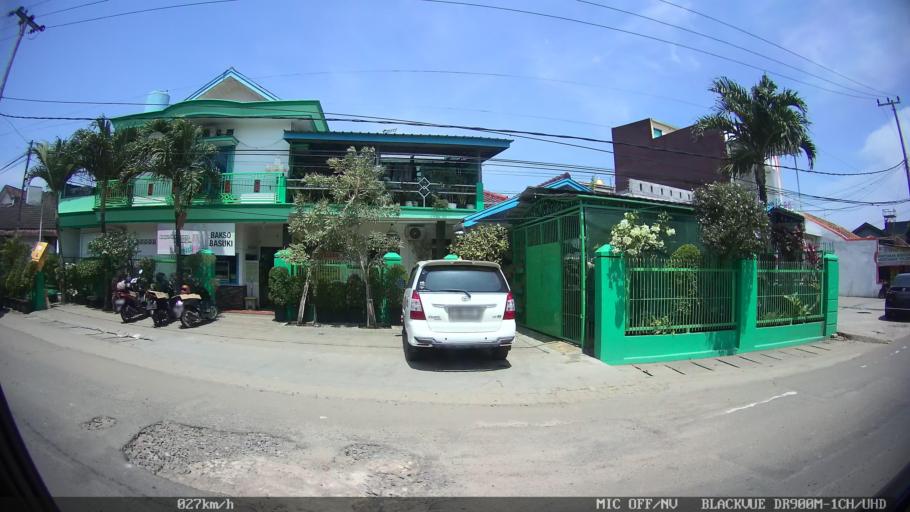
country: ID
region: Lampung
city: Kedaton
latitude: -5.3896
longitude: 105.2816
